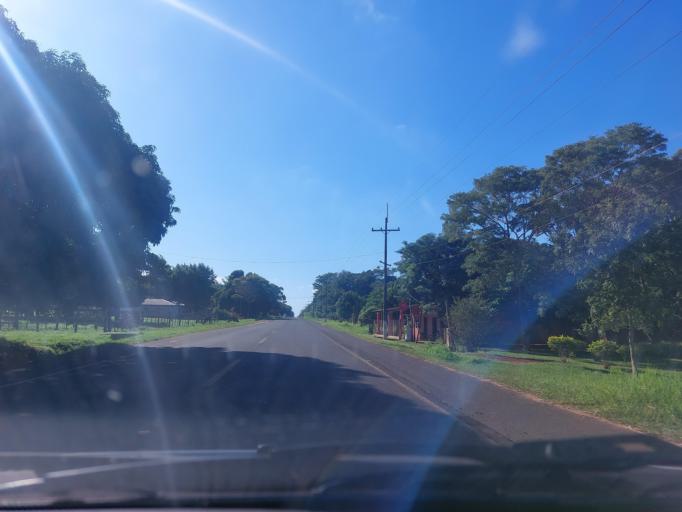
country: PY
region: San Pedro
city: Guayaybi
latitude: -24.5317
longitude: -56.4725
